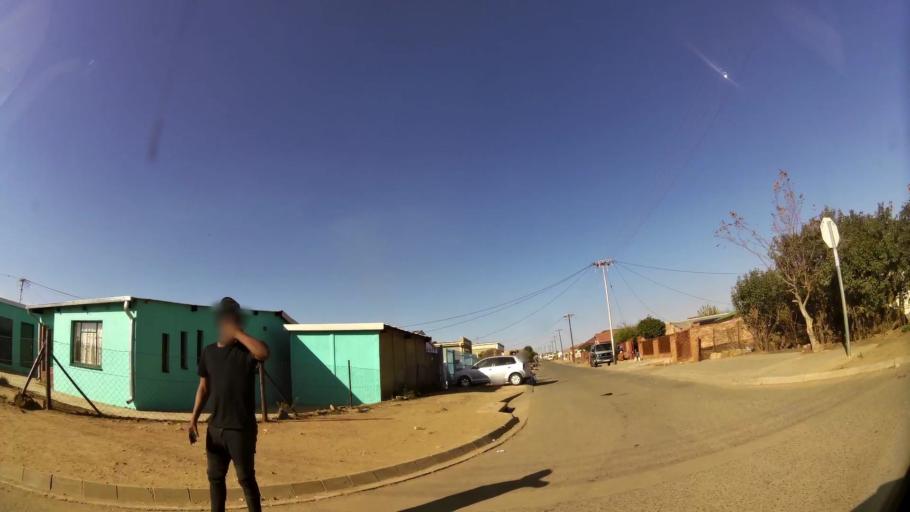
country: ZA
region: Gauteng
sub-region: City of Tshwane Metropolitan Municipality
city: Cullinan
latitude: -25.7194
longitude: 28.3808
